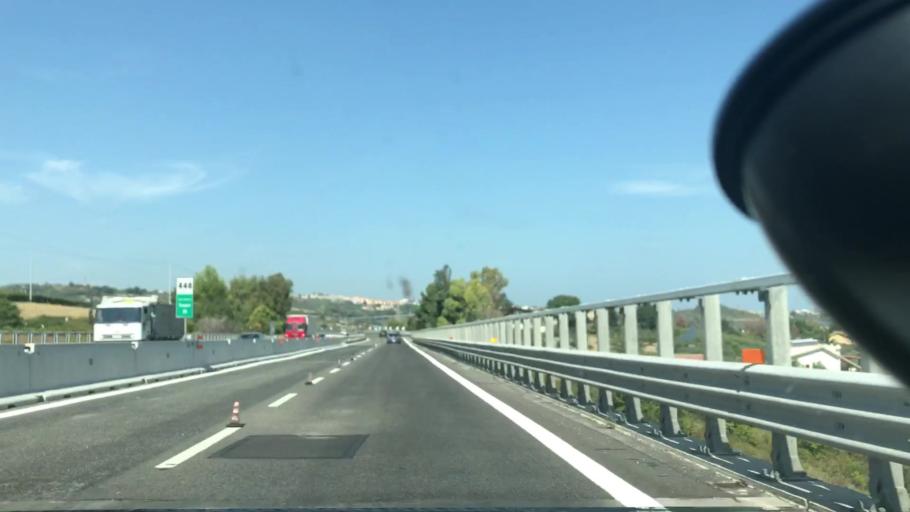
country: IT
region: Abruzzo
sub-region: Provincia di Chieti
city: Marina di Vasto
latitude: 42.0760
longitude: 14.7123
